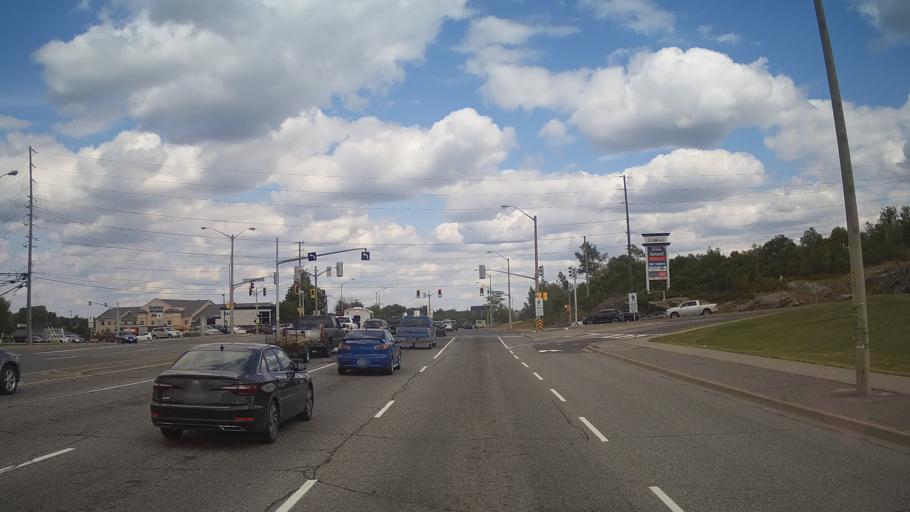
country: CA
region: Ontario
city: Greater Sudbury
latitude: 46.5051
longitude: -80.9453
